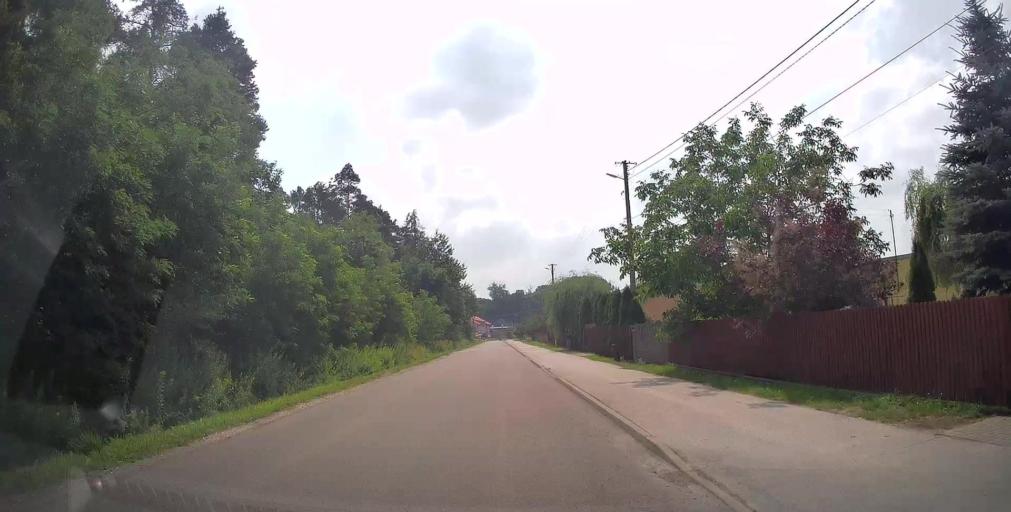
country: PL
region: Masovian Voivodeship
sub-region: Powiat bialobrzeski
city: Sucha
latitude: 51.6247
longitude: 20.9530
